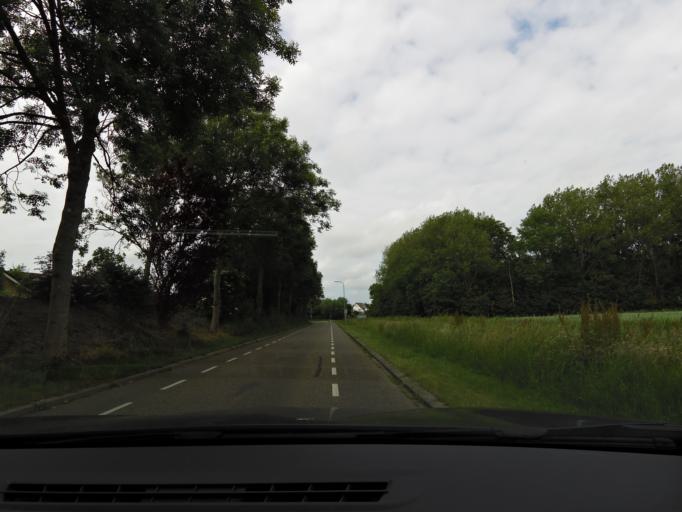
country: NL
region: Zeeland
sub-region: Gemeente Middelburg
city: Middelburg
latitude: 51.5619
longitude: 3.5048
